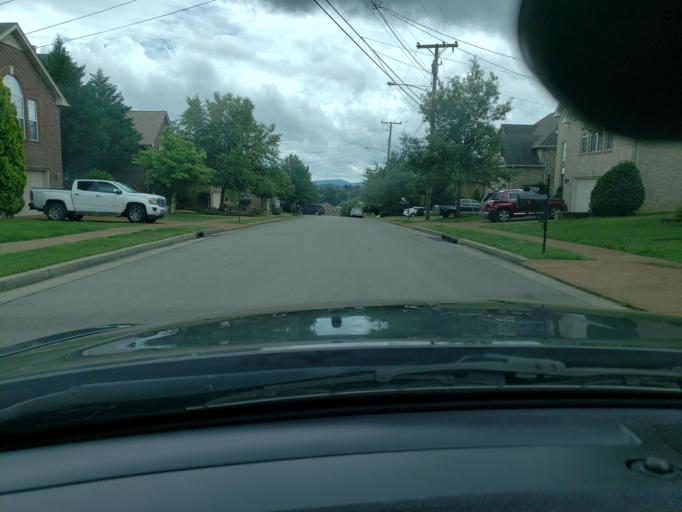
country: US
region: Tennessee
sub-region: Williamson County
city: Nolensville
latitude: 36.0170
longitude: -86.6984
